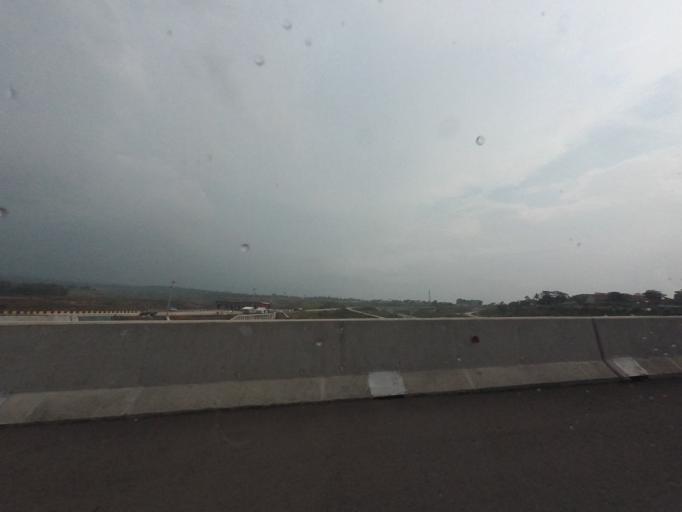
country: ID
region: West Java
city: Cicurug
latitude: -6.7517
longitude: 106.8026
